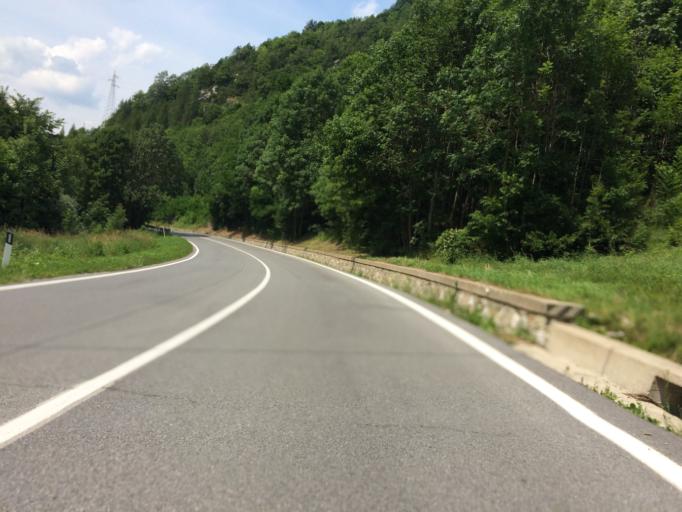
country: IT
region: Piedmont
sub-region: Provincia di Cuneo
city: Vernante
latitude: 44.2305
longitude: 7.5557
